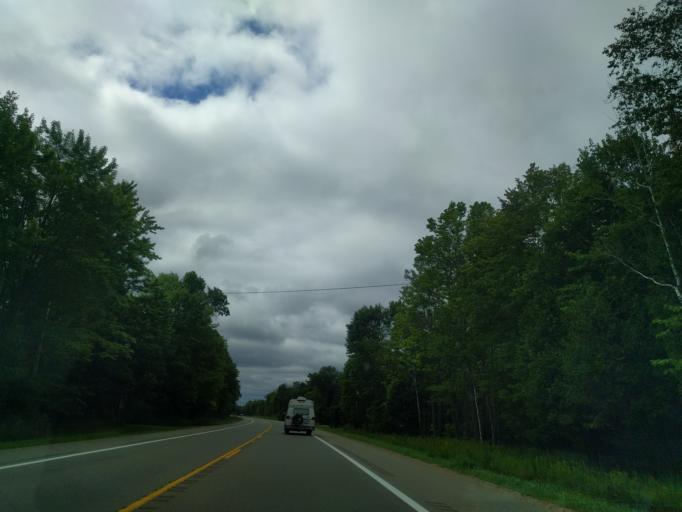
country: US
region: Michigan
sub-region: Menominee County
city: Menominee
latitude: 45.2726
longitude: -87.4679
